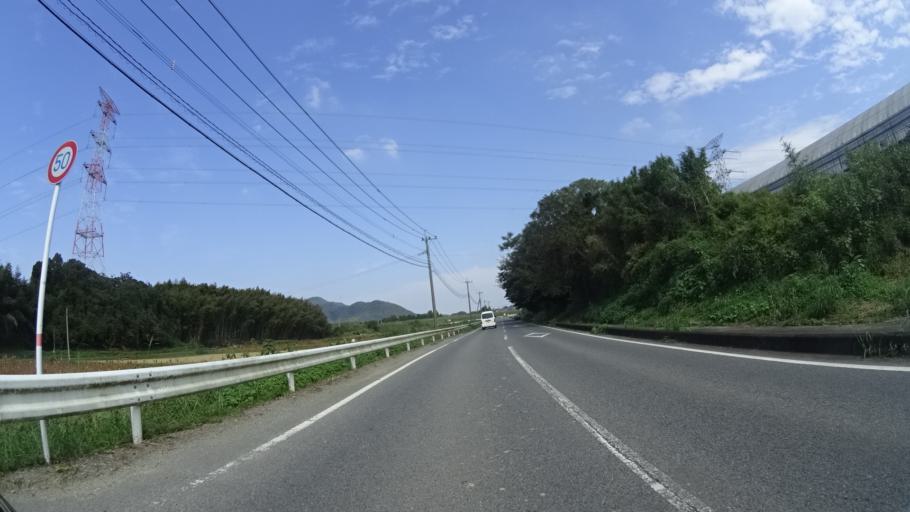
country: JP
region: Kumamoto
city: Matsubase
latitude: 32.6605
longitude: 130.7155
